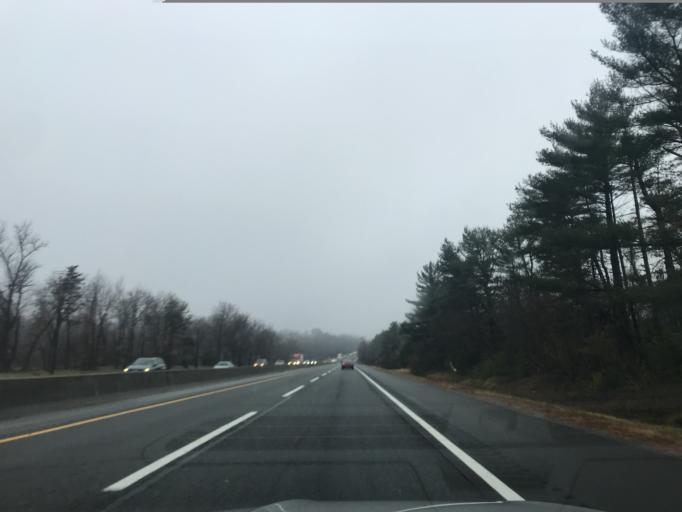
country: US
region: New Jersey
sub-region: Gloucester County
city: Beckett
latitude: 39.7143
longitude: -75.3474
